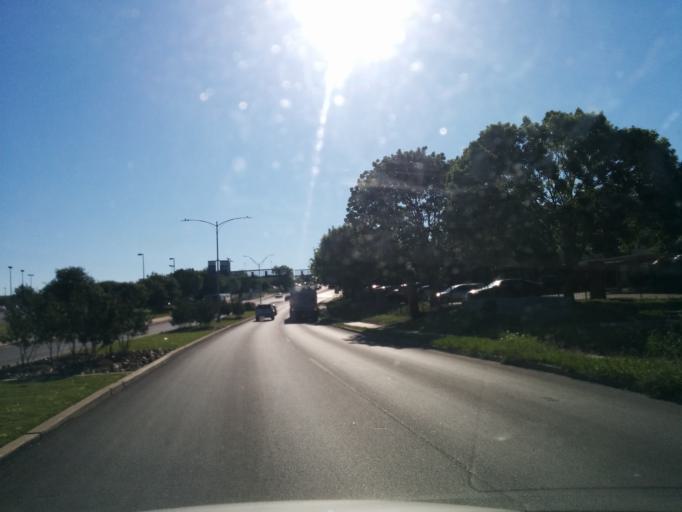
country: US
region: Texas
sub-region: Bexar County
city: Leon Valley
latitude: 29.5110
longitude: -98.5861
